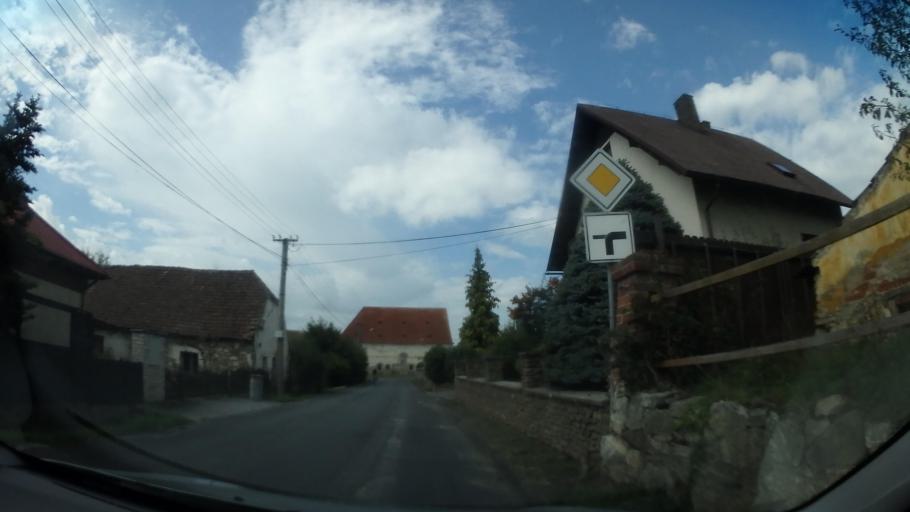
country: CZ
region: Plzensky
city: Horazd'ovice
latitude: 49.2669
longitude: 13.6320
